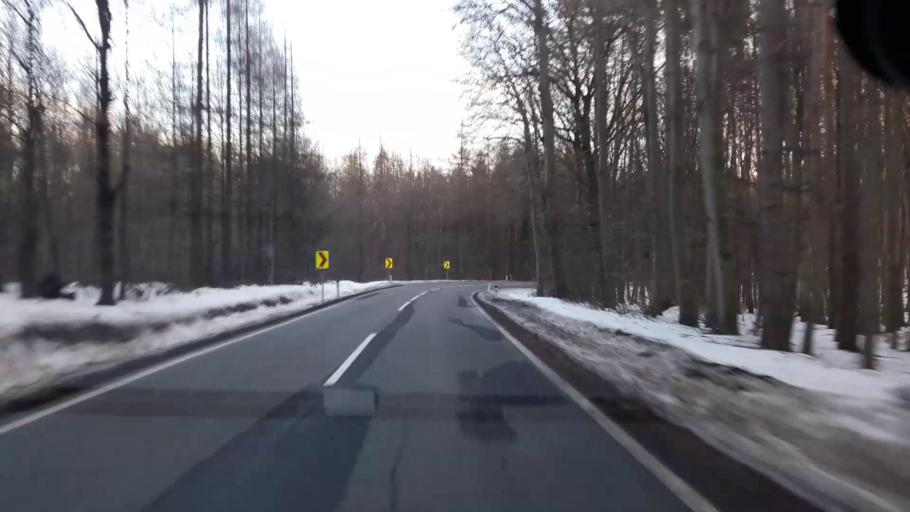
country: AT
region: Lower Austria
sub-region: Politischer Bezirk Wien-Umgebung
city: Mauerbach
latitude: 48.2760
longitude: 16.1831
